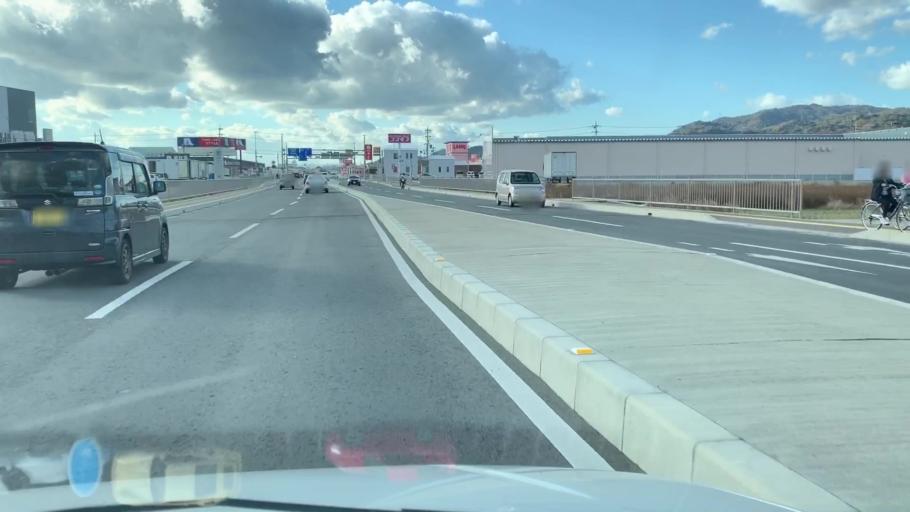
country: JP
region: Wakayama
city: Wakayama-shi
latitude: 34.2613
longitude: 135.2203
